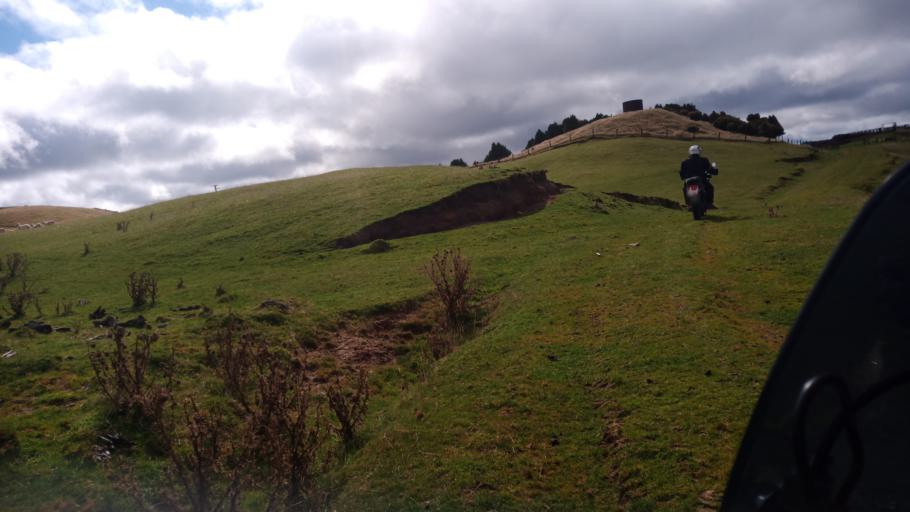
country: NZ
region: Gisborne
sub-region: Gisborne District
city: Gisborne
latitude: -38.4739
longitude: 177.5390
